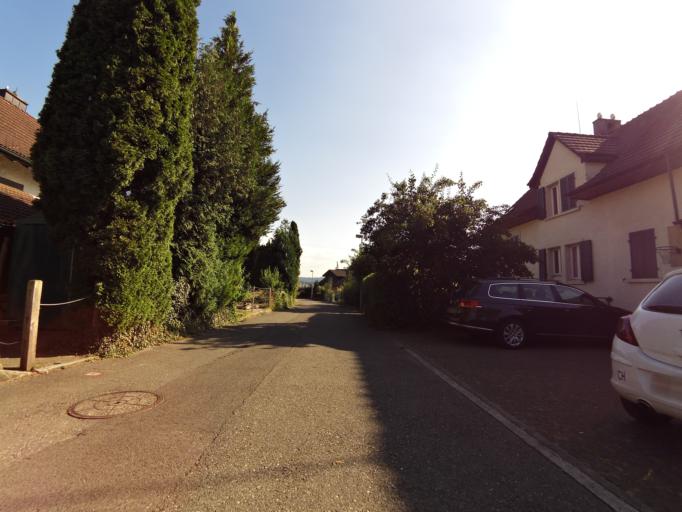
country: CH
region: Aargau
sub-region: Bezirk Lenzburg
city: Niederlenz
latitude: 47.3978
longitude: 8.1816
